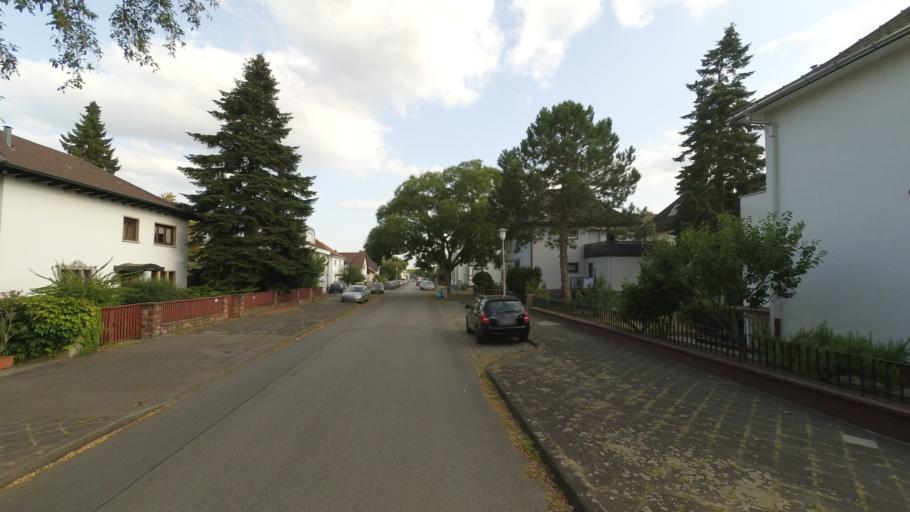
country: DE
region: Rheinland-Pfalz
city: Altrip
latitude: 49.4339
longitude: 8.5305
